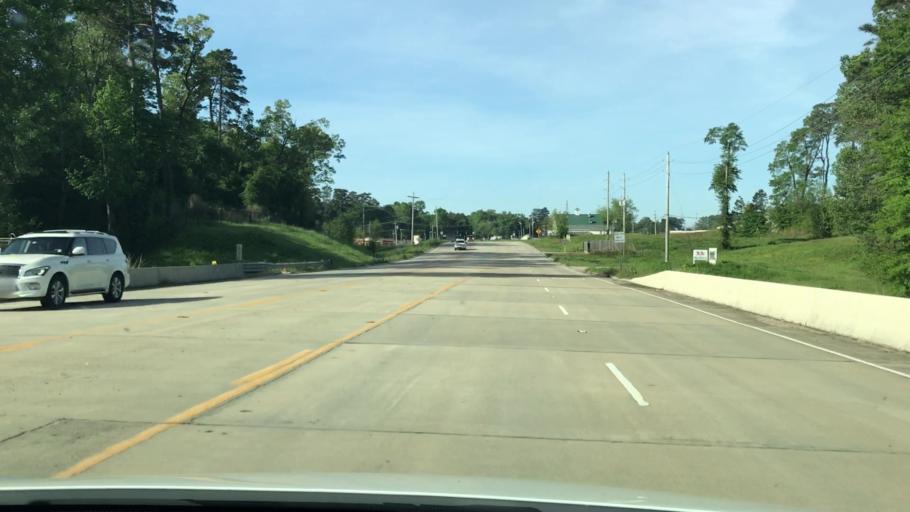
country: US
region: Louisiana
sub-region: Bossier Parish
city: Bossier City
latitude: 32.3972
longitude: -93.7231
